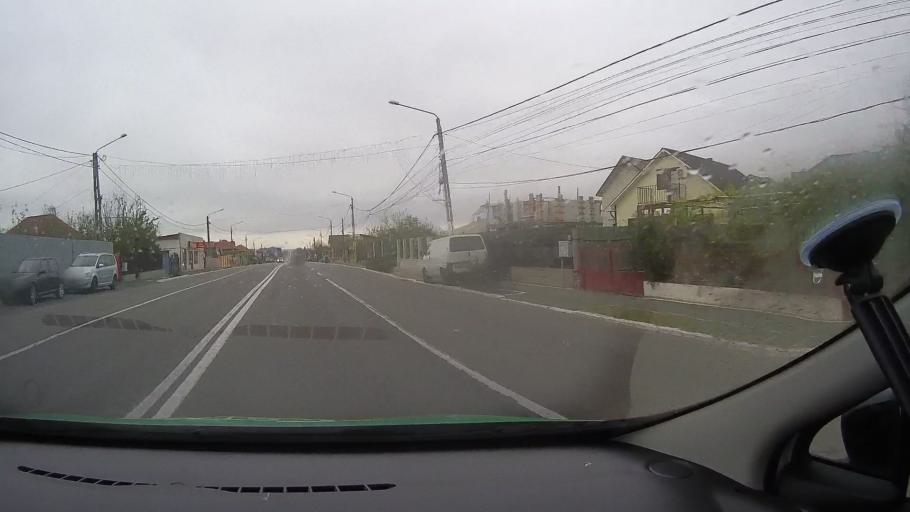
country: RO
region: Constanta
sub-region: Comuna Valu lui Traian
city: Valu lui Traian
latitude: 44.1648
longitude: 28.4717
